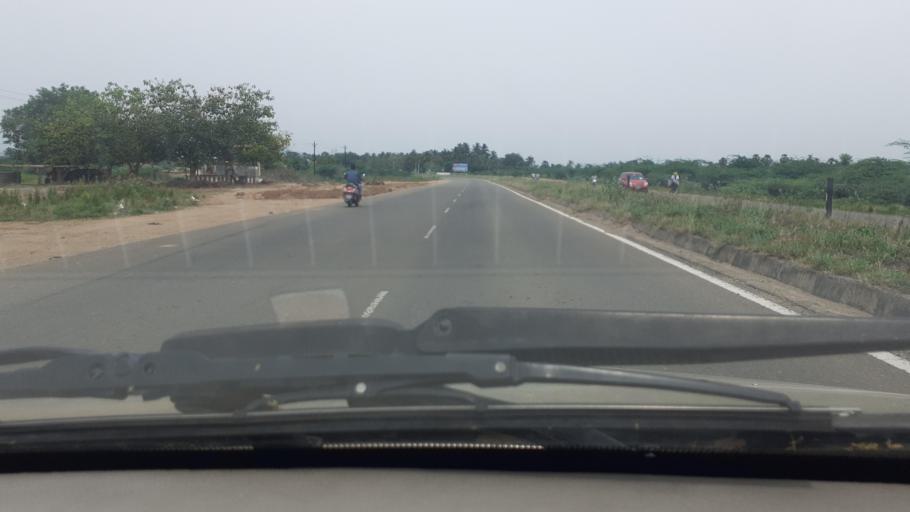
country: IN
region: Tamil Nadu
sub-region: Tirunelveli Kattabo
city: Tirunelveli
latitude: 8.7096
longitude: 77.8091
